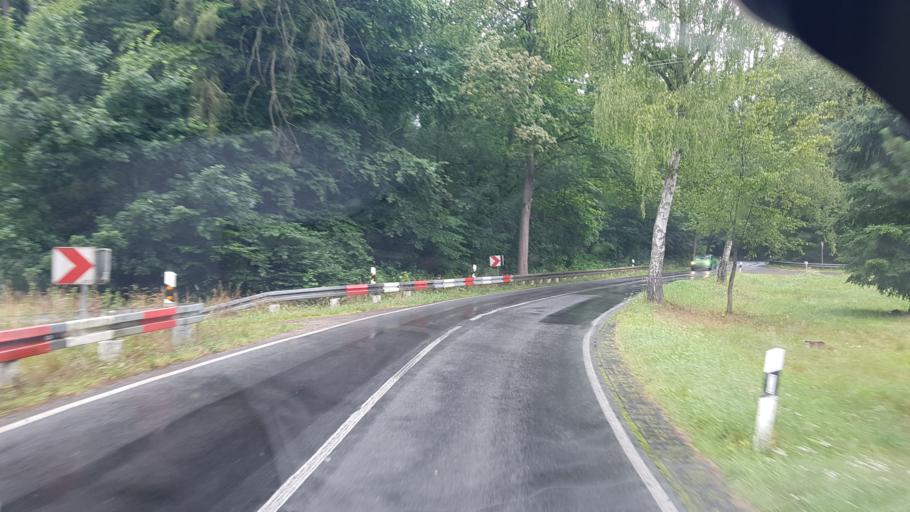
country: DE
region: Brandenburg
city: Lebusa
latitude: 51.7807
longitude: 13.3857
